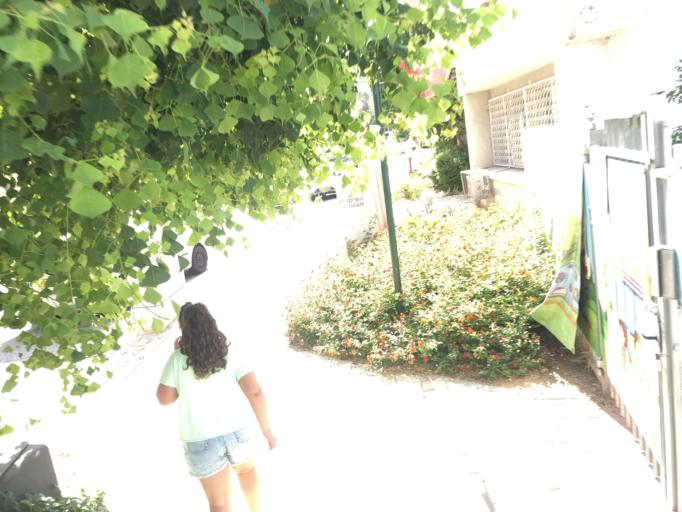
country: IL
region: Central District
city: Yehud
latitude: 32.0294
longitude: 34.8875
